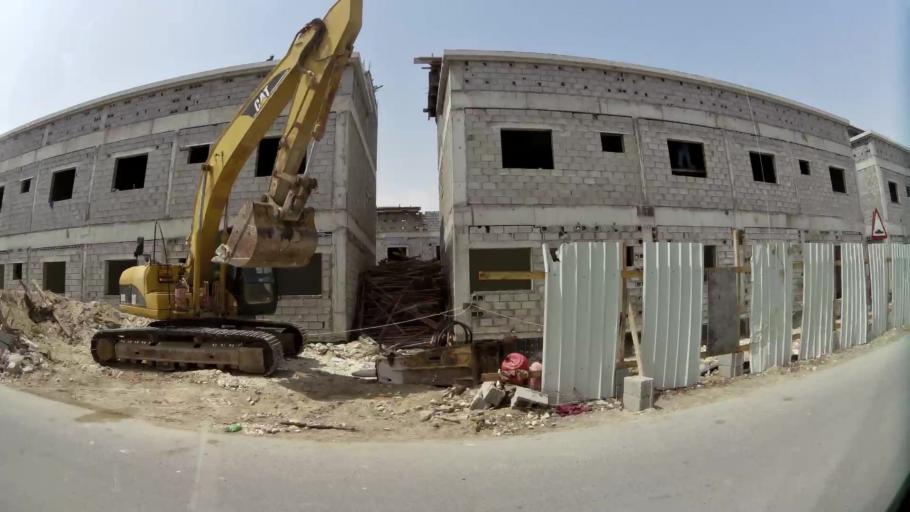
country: QA
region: Baladiyat ar Rayyan
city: Ar Rayyan
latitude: 25.2455
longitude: 51.4224
